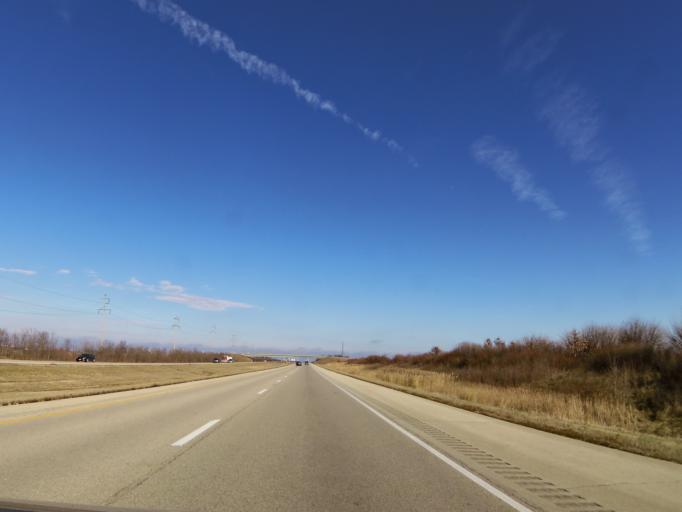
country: US
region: Illinois
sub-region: LaSalle County
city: Mendota
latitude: 41.6660
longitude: -89.0580
